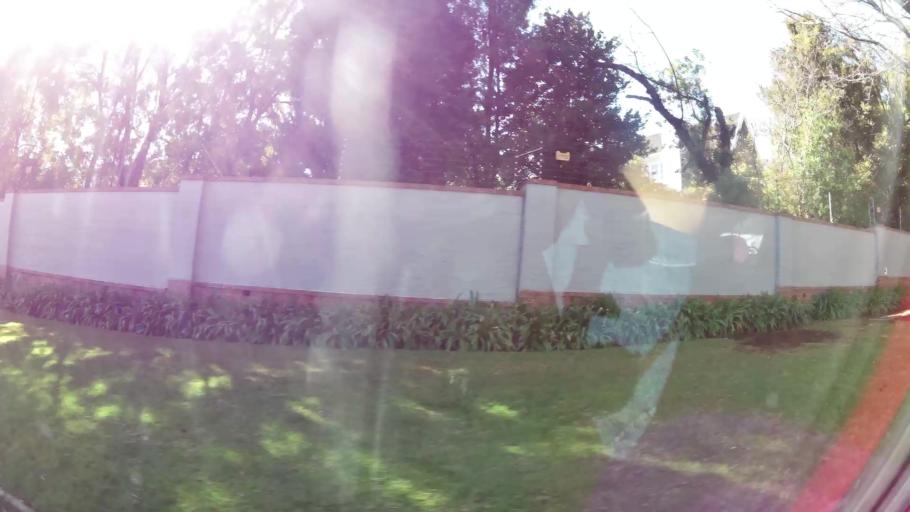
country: ZA
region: Gauteng
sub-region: City of Johannesburg Metropolitan Municipality
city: Johannesburg
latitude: -26.1602
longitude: 28.0382
